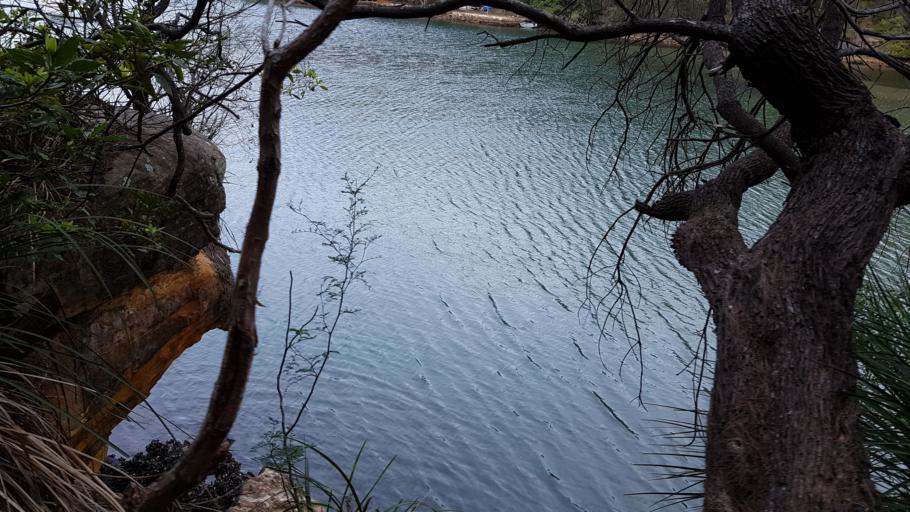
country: AU
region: New South Wales
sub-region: Willoughby
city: Castlecrag
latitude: -33.7963
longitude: 151.2216
